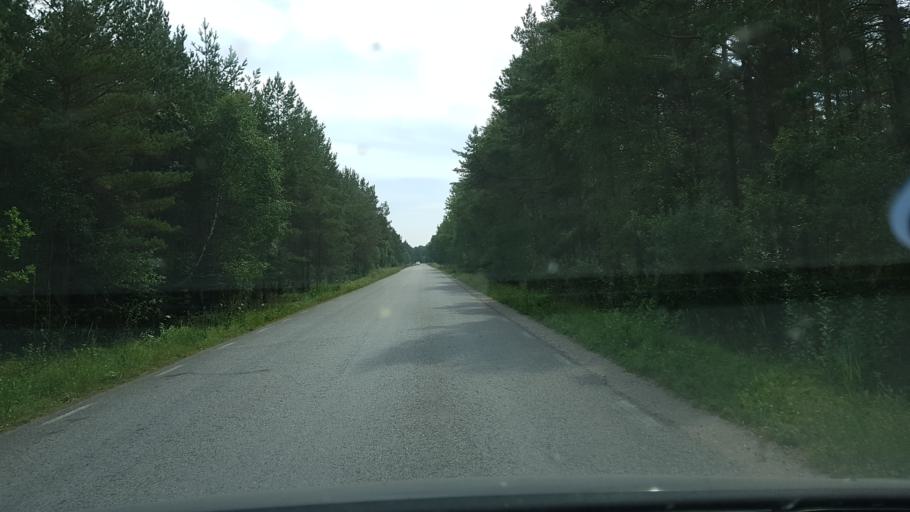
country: SE
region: Gotland
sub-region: Gotland
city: Visby
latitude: 57.7231
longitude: 18.5081
